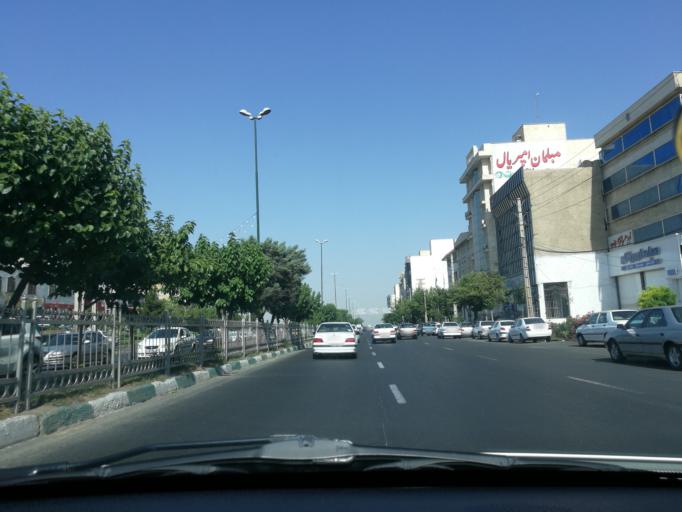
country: IR
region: Alborz
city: Karaj
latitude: 35.8309
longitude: 51.0067
